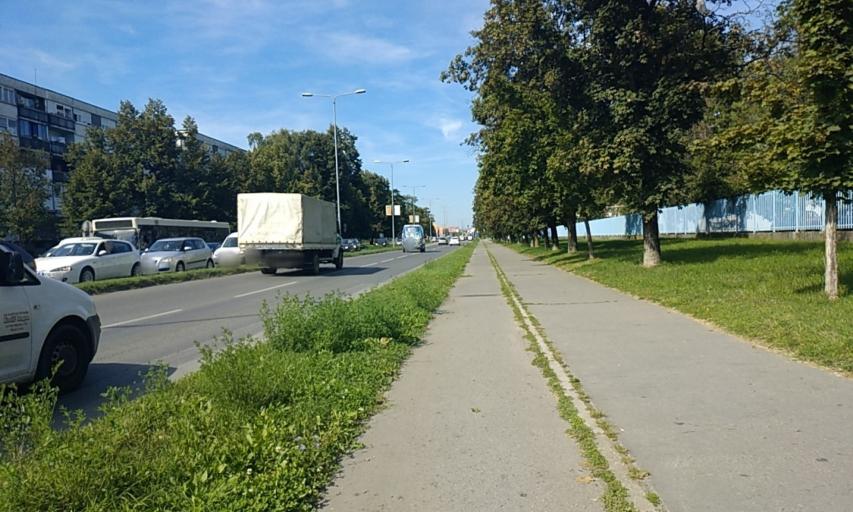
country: BA
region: Republika Srpska
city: Starcevica
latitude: 44.7724
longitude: 17.2091
